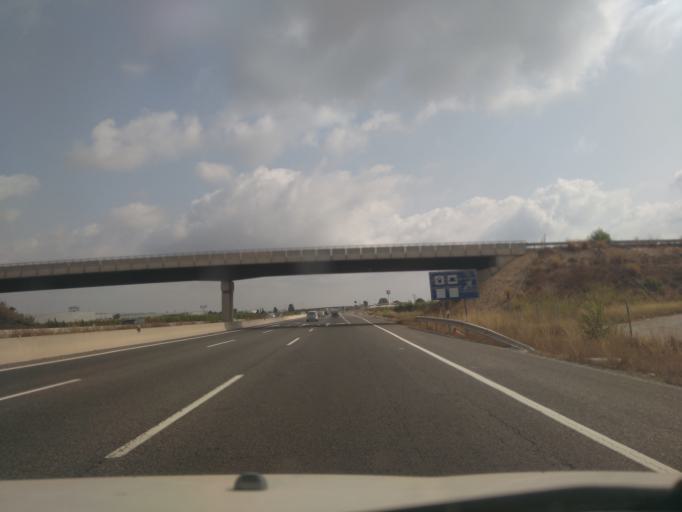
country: ES
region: Valencia
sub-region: Provincia de Valencia
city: L'Alcudia
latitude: 39.2221
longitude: -0.4915
